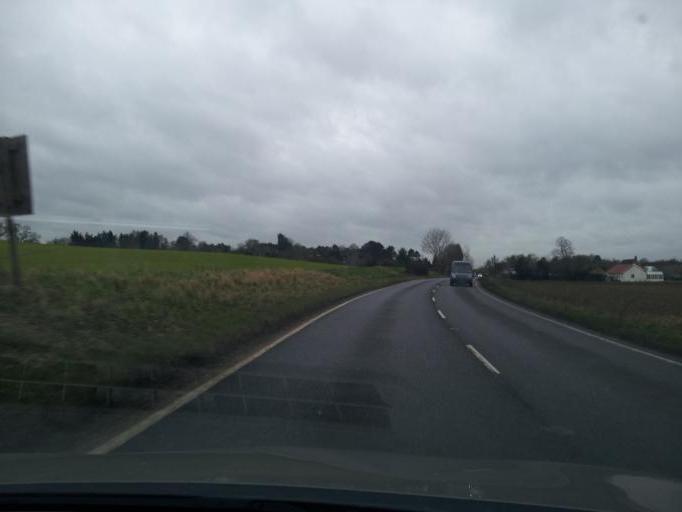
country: GB
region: England
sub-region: Suffolk
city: Botesdale
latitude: 52.3352
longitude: 0.9586
